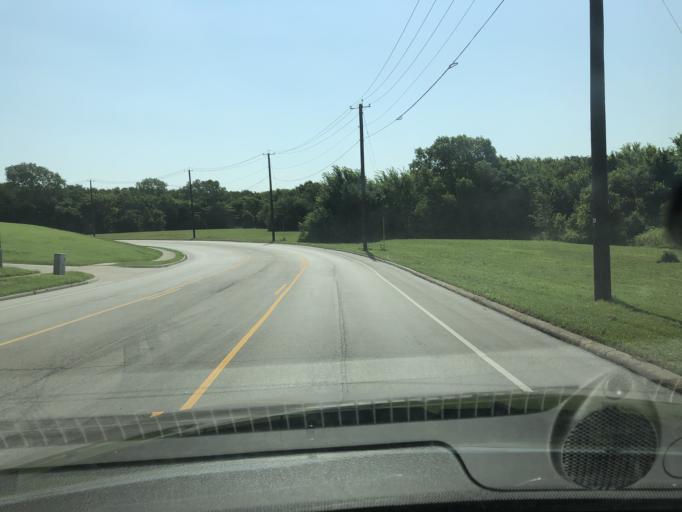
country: US
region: Texas
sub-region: Dallas County
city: Sunnyvale
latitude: 32.8355
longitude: -96.5827
